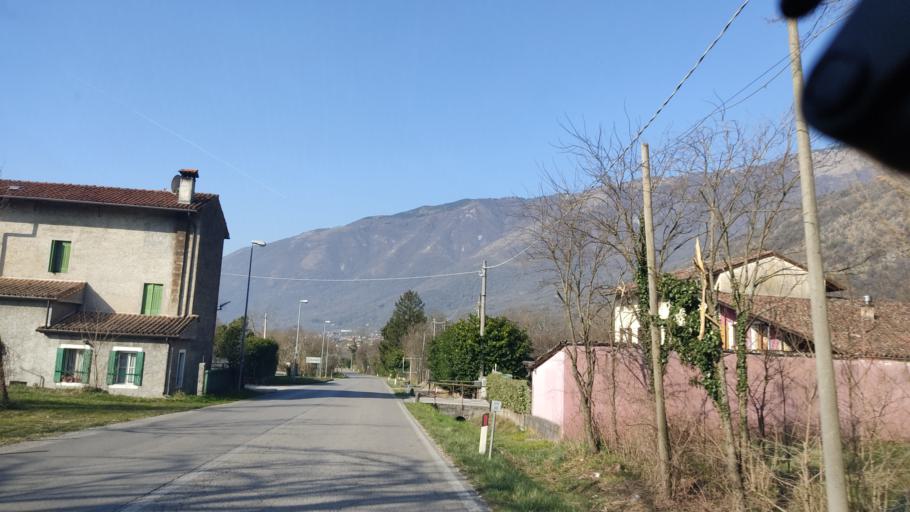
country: IT
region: Friuli Venezia Giulia
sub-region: Provincia di Pordenone
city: Polcenigo
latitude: 46.0406
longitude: 12.5067
